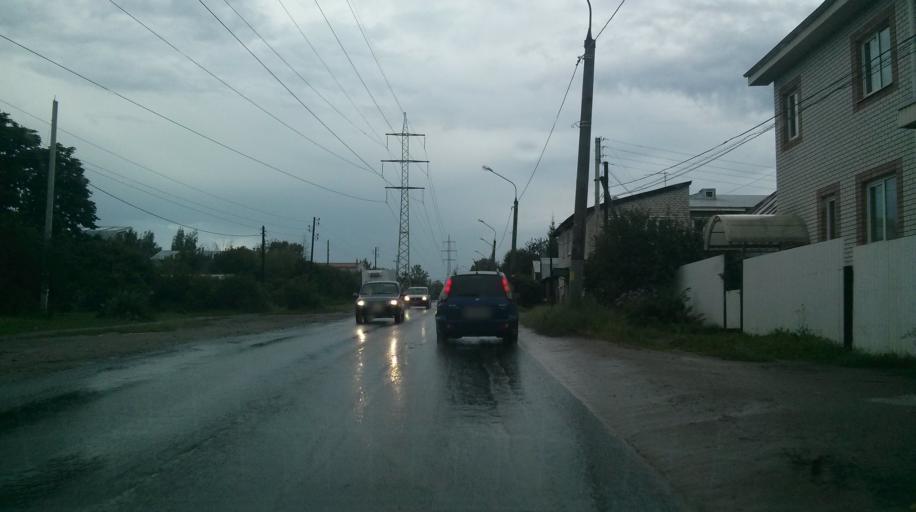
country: RU
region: Nizjnij Novgorod
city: Nizhniy Novgorod
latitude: 56.2567
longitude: 43.9955
